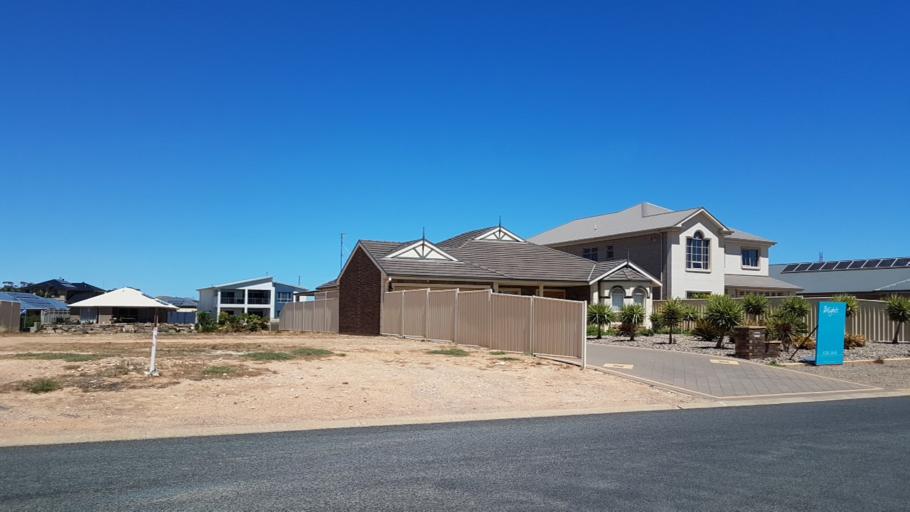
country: AU
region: South Australia
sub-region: Copper Coast
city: Wallaroo
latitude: -33.9209
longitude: 137.6382
